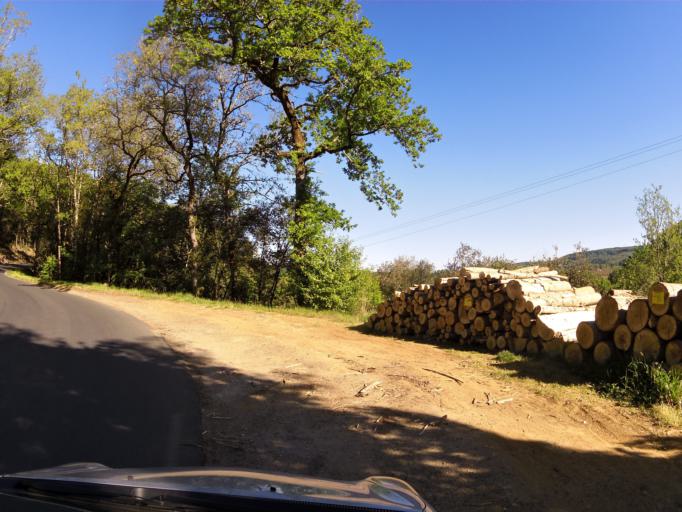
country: FR
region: Aquitaine
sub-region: Departement de la Dordogne
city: Carsac-Aillac
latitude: 44.8447
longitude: 1.2550
